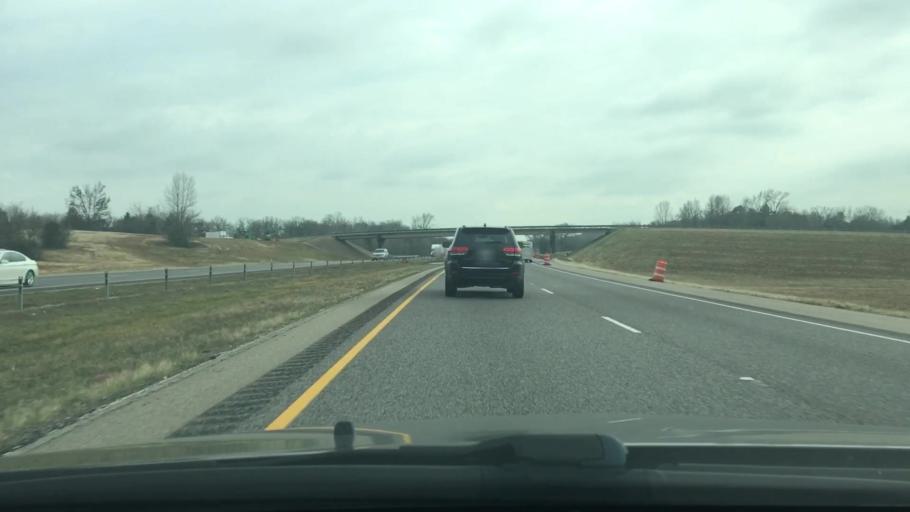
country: US
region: Texas
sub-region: Leon County
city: Buffalo
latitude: 31.5017
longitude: -96.0978
